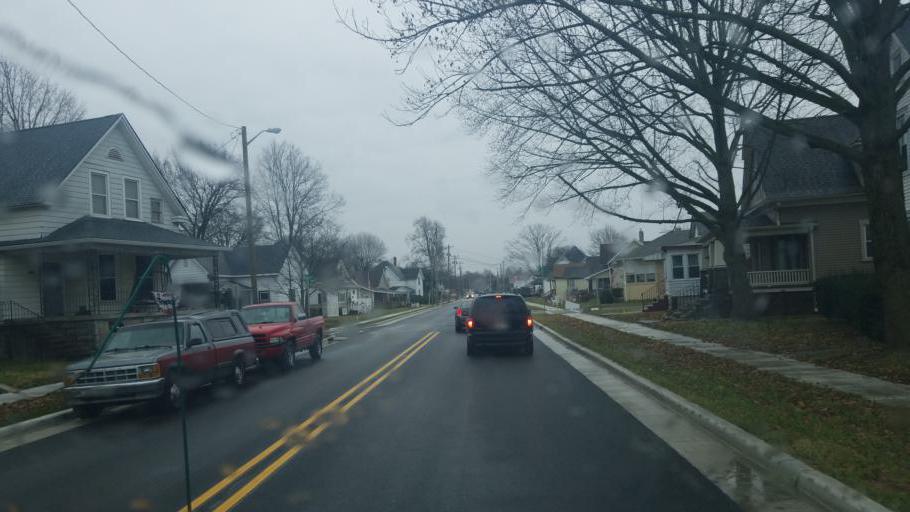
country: US
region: Indiana
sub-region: Shelby County
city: Shelbyville
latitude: 39.5152
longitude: -85.7751
